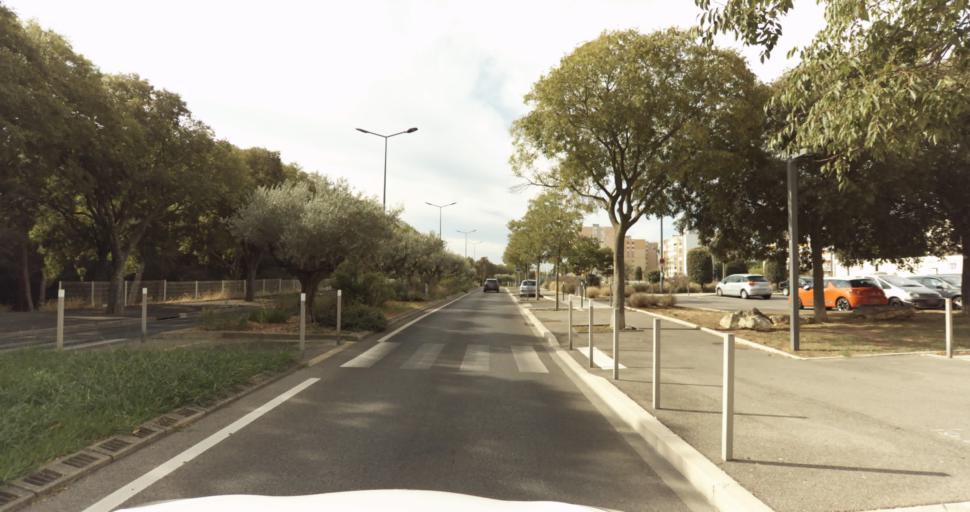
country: FR
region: Provence-Alpes-Cote d'Azur
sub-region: Departement des Bouches-du-Rhone
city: Miramas
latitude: 43.5955
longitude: 5.0112
